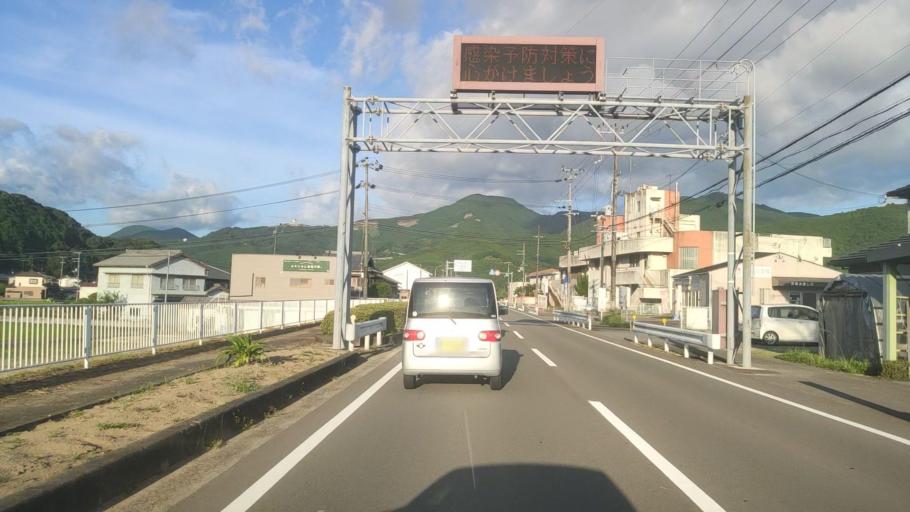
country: JP
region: Wakayama
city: Tanabe
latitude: 33.7158
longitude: 135.4629
